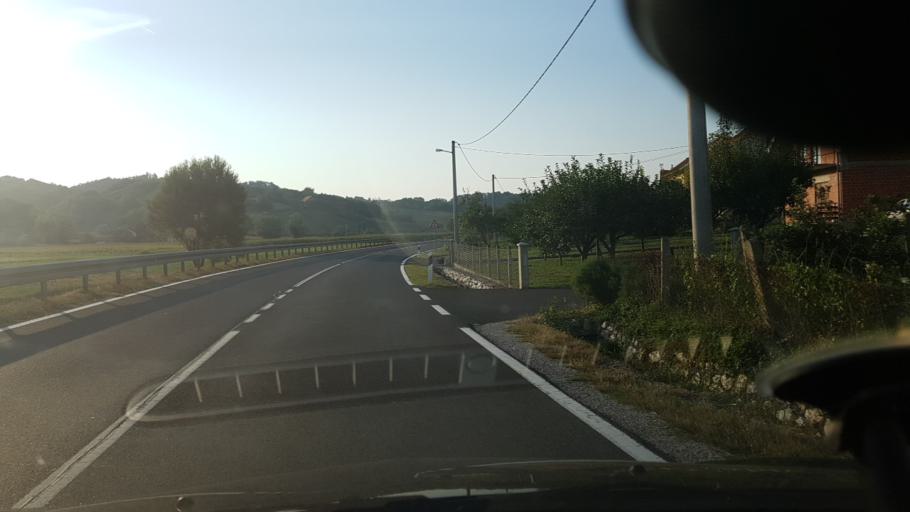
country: HR
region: Krapinsko-Zagorska
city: Pregrada
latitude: 46.1140
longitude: 15.8093
